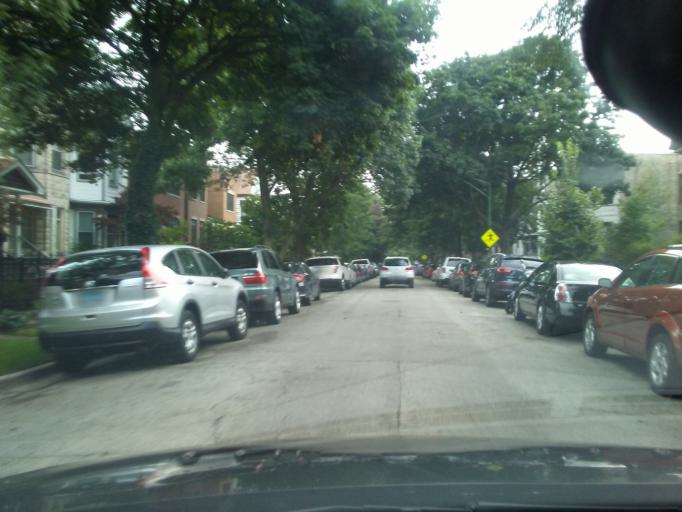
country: US
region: Illinois
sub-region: Cook County
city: Lincolnwood
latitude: 41.9570
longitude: -87.6767
